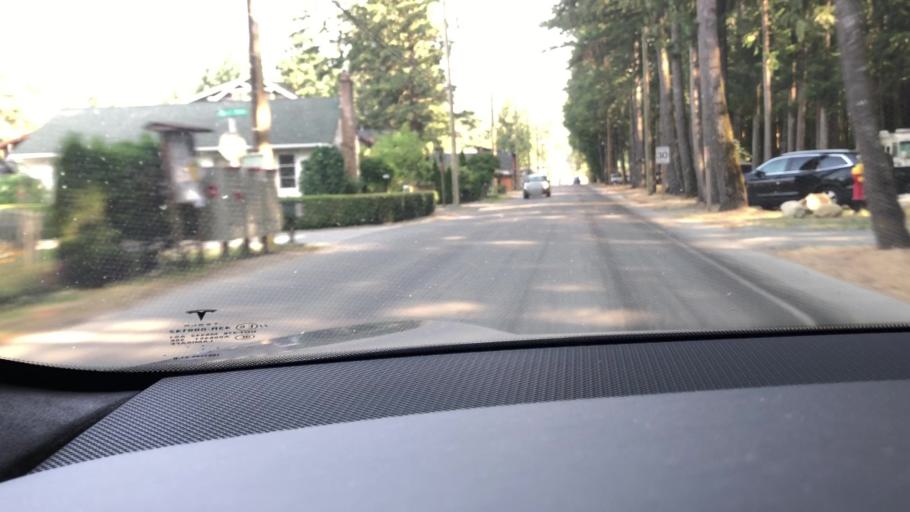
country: CA
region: British Columbia
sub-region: Fraser Valley Regional District
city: Chilliwack
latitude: 49.0697
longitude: -121.9761
